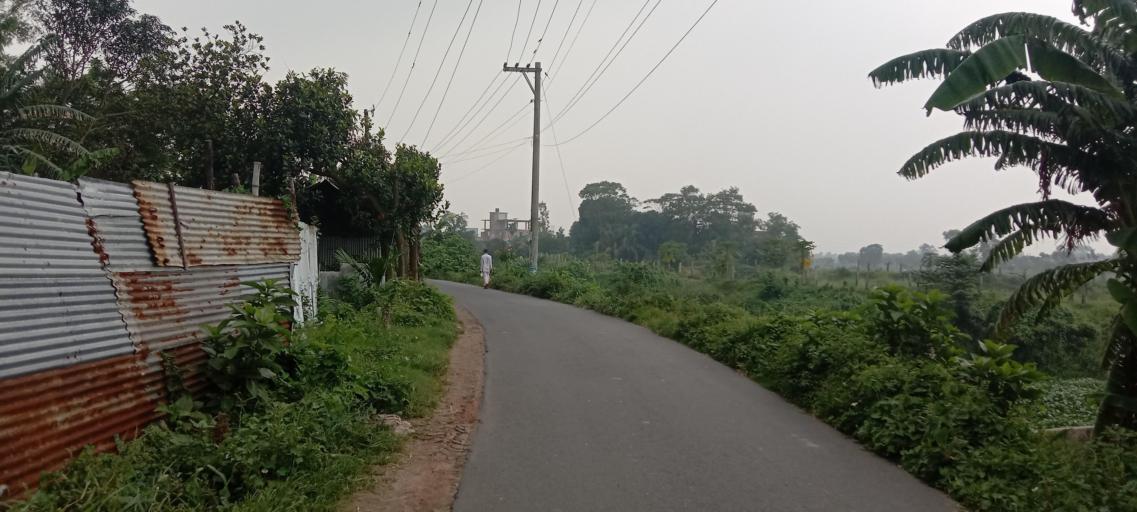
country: BD
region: Dhaka
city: Azimpur
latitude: 23.7392
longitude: 90.3168
